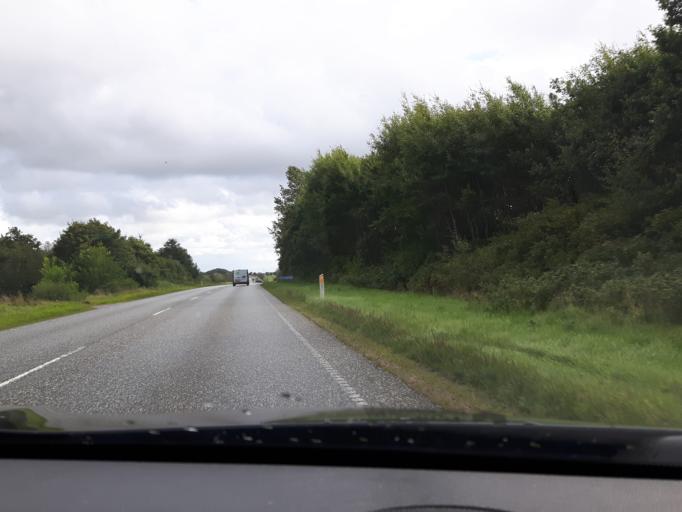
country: DK
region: Central Jutland
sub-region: Herning Kommune
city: Avlum
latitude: 56.2759
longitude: 8.7593
